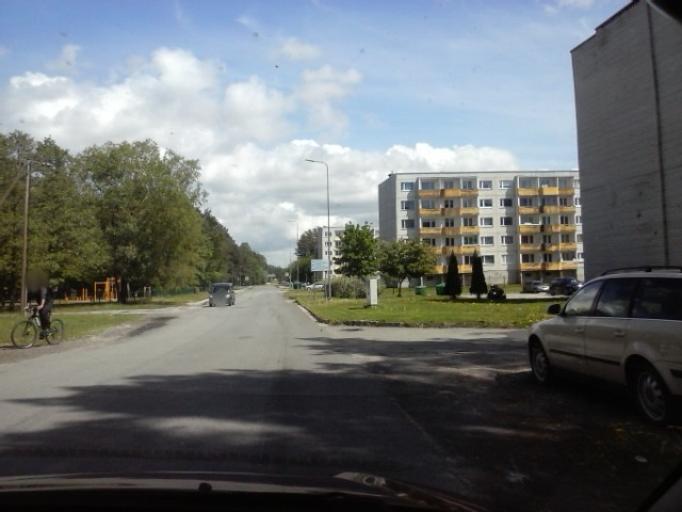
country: EE
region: Laeaene
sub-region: Haapsalu linn
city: Haapsalu
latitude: 58.9337
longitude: 23.5524
